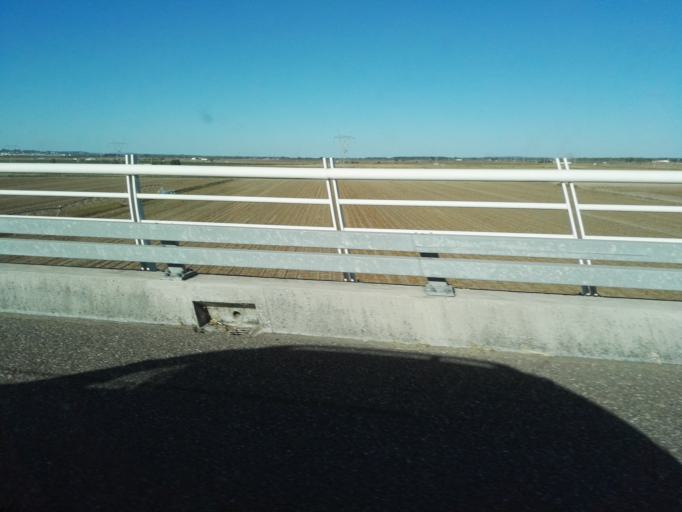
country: PT
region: Santarem
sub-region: Benavente
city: Samora Correia
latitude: 38.9889
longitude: -8.8929
